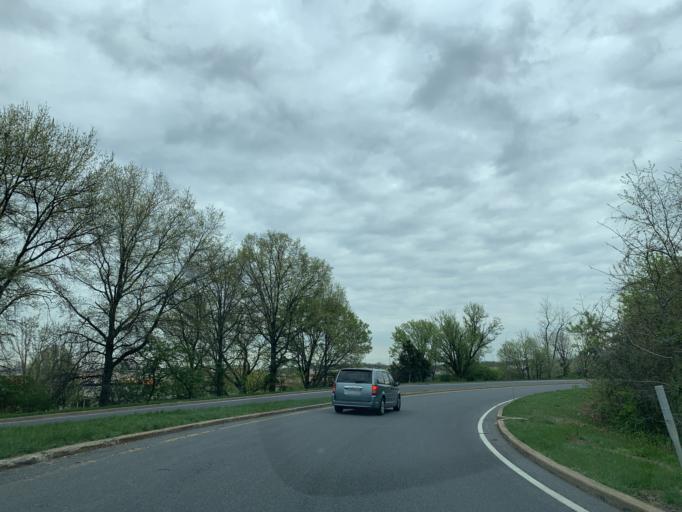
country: US
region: Maryland
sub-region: Washington County
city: Hagerstown
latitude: 39.6540
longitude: -77.7513
